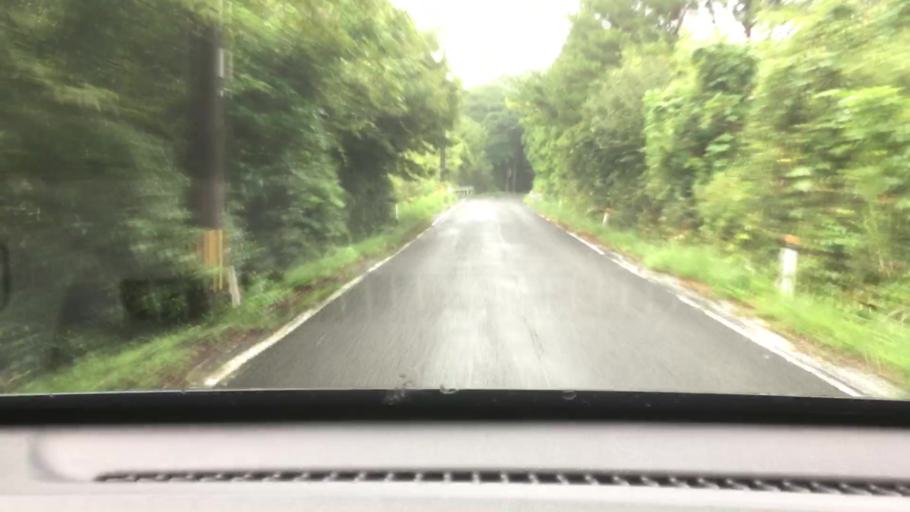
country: JP
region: Nagasaki
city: Togitsu
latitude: 32.9230
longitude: 129.7215
